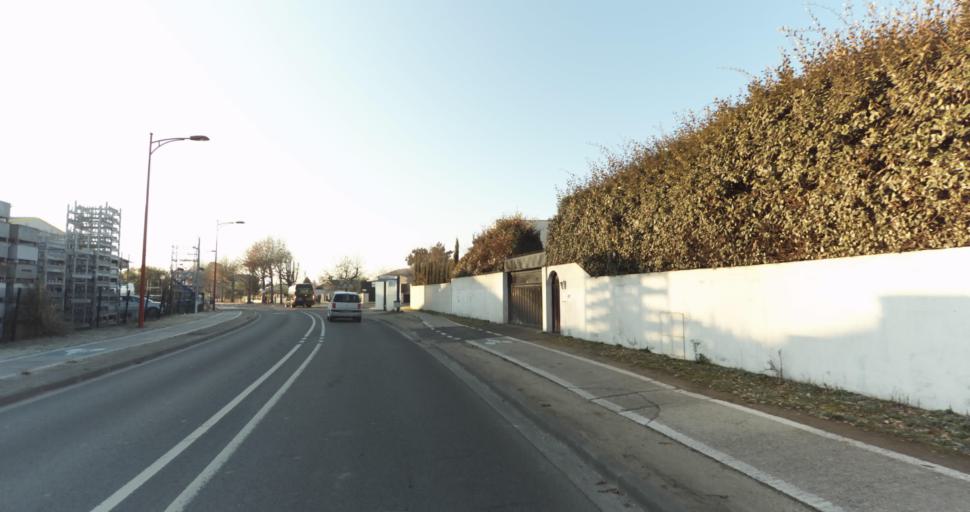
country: FR
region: Aquitaine
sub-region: Departement de la Gironde
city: Carbon-Blanc
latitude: 44.9096
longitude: -0.4959
